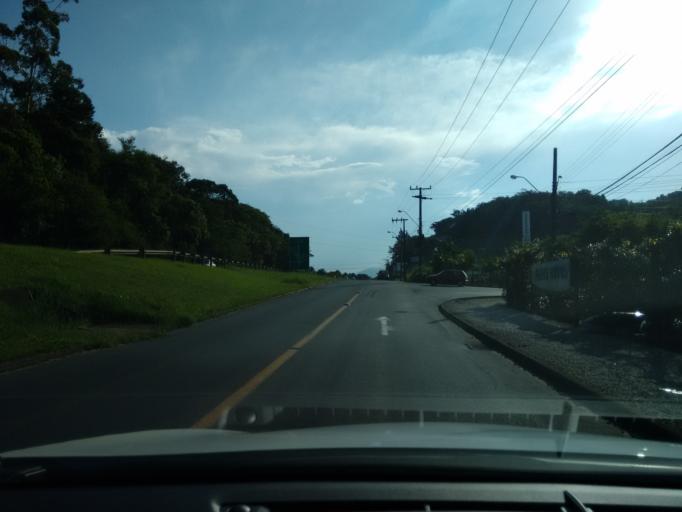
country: BR
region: Santa Catarina
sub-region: Blumenau
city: Blumenau
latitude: -26.8634
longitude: -49.0975
